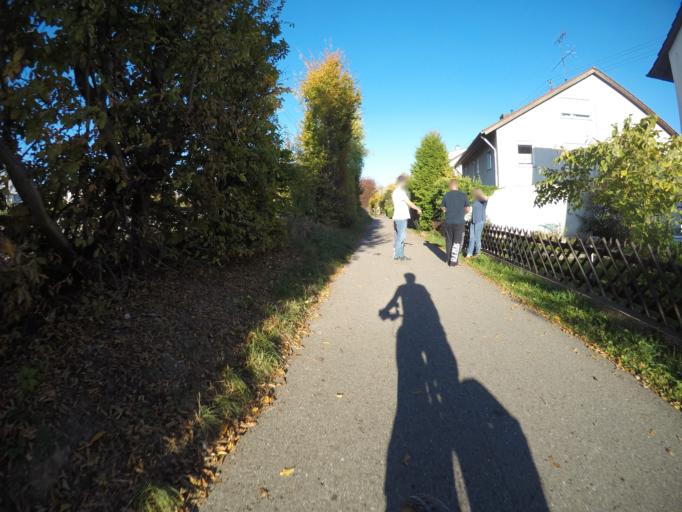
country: DE
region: Baden-Wuerttemberg
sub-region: Regierungsbezirk Stuttgart
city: Nufringen
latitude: 48.6189
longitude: 8.8880
